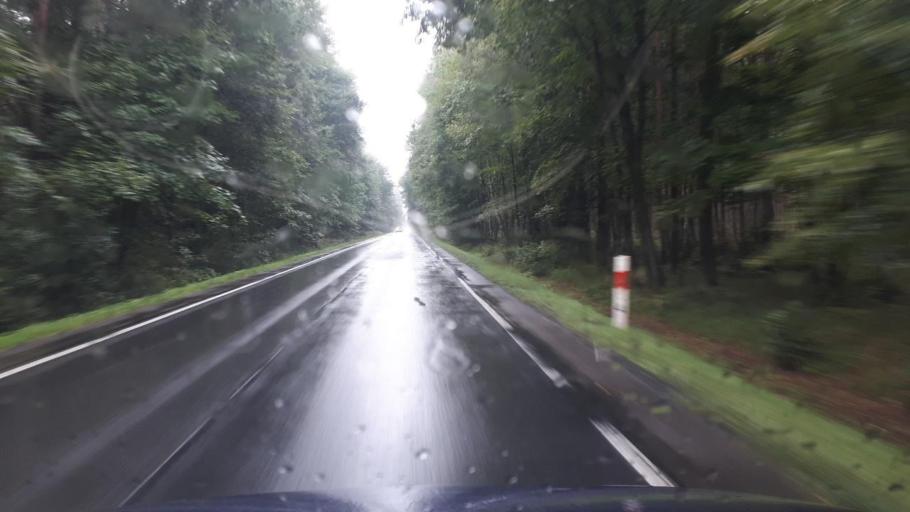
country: PL
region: Silesian Voivodeship
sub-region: Powiat tarnogorski
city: Tworog
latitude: 50.5308
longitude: 18.6988
